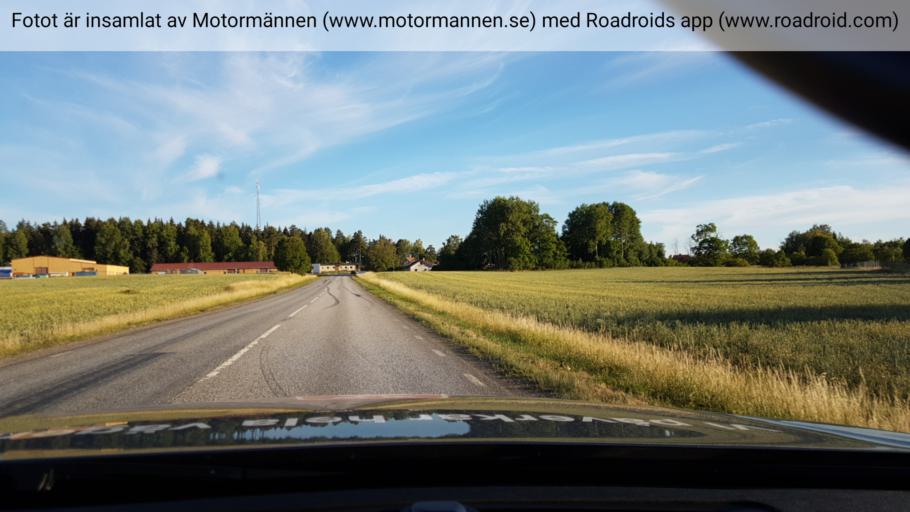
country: SE
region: Vaestmanland
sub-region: Vasteras
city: Skultuna
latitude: 59.7277
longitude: 16.4328
